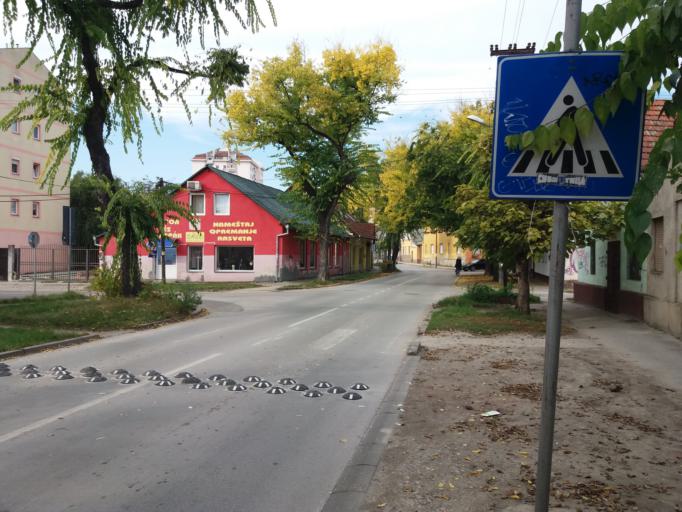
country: RS
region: Autonomna Pokrajina Vojvodina
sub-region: Severnobacki Okrug
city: Subotica
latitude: 46.1052
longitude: 19.6634
